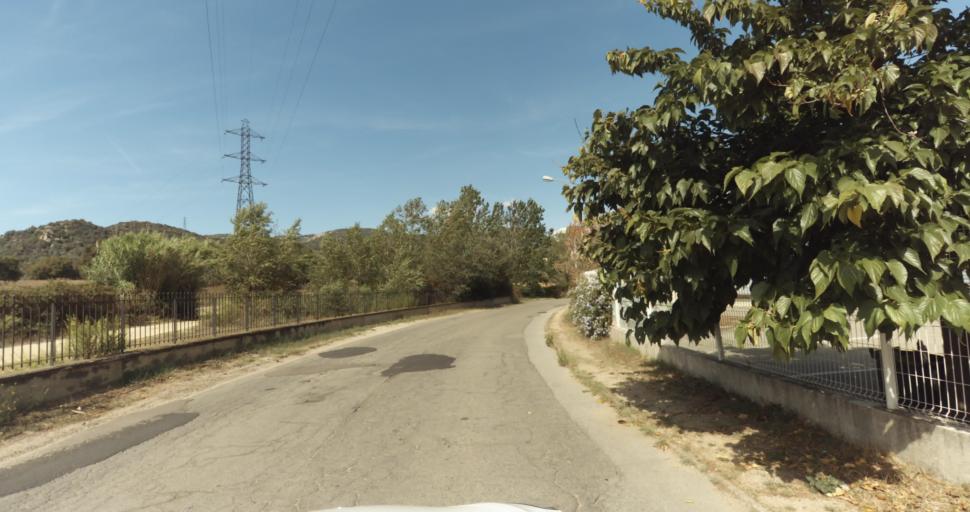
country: FR
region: Corsica
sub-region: Departement de la Corse-du-Sud
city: Ajaccio
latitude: 41.9485
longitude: 8.7629
